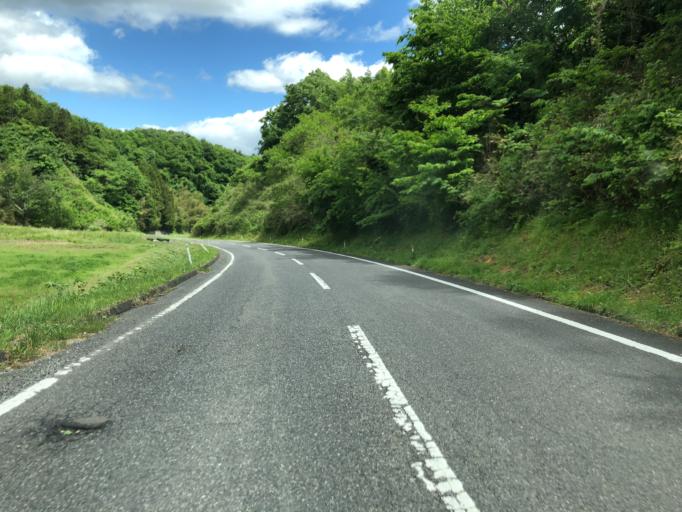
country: JP
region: Fukushima
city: Nihommatsu
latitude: 37.5326
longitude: 140.4689
